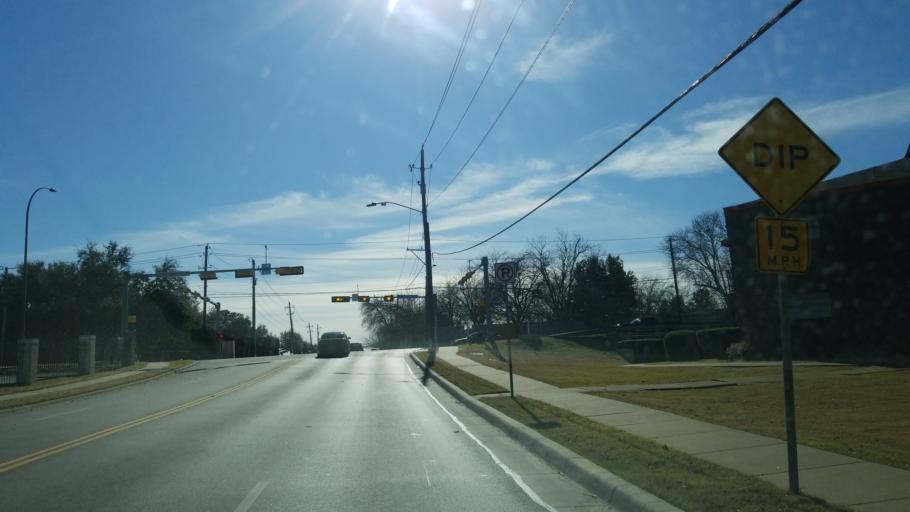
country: US
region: Texas
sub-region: Tarrant County
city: Arlington
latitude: 32.7213
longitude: -97.0572
